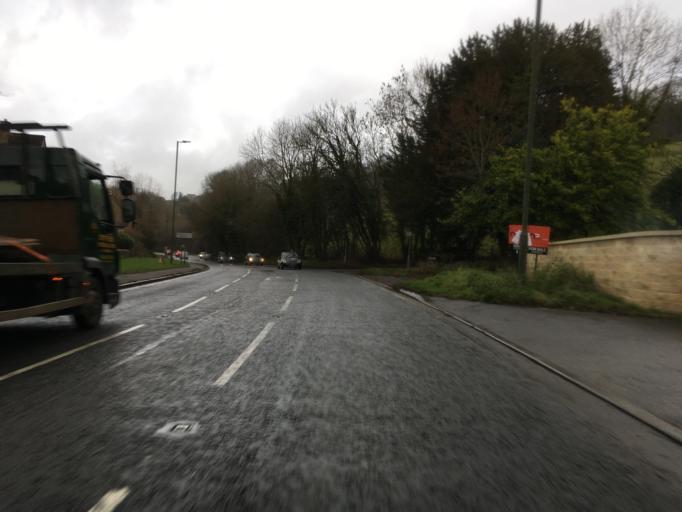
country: GB
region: England
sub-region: Gloucestershire
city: Nailsworth
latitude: 51.7228
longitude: -2.2280
